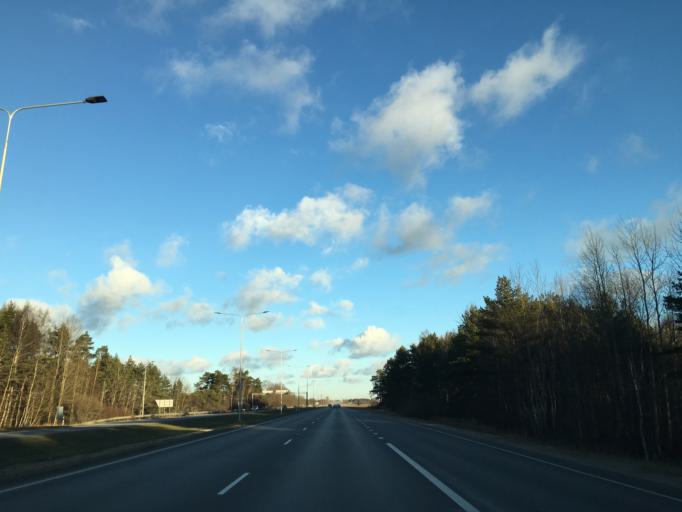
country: EE
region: Harju
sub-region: Saue linn
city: Saue
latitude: 59.3160
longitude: 24.5795
